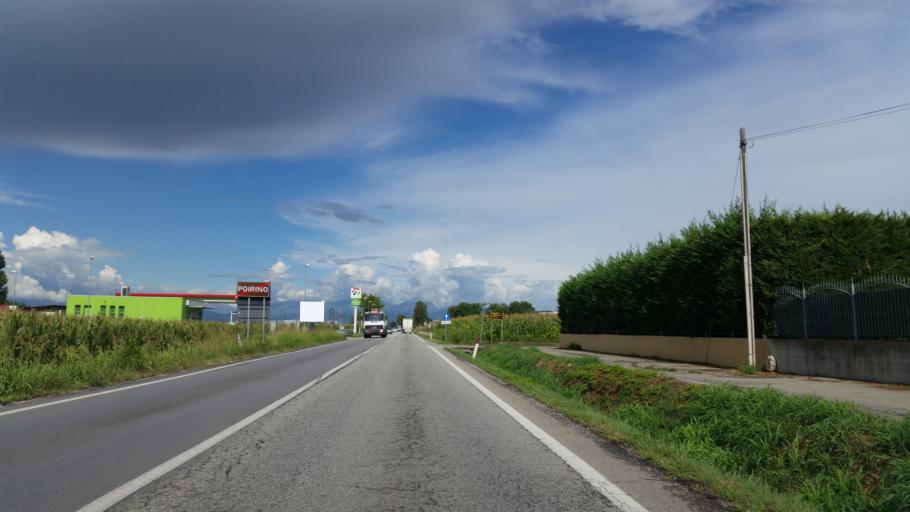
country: IT
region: Piedmont
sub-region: Provincia di Torino
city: Marocchi
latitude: 44.9464
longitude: 7.8082
